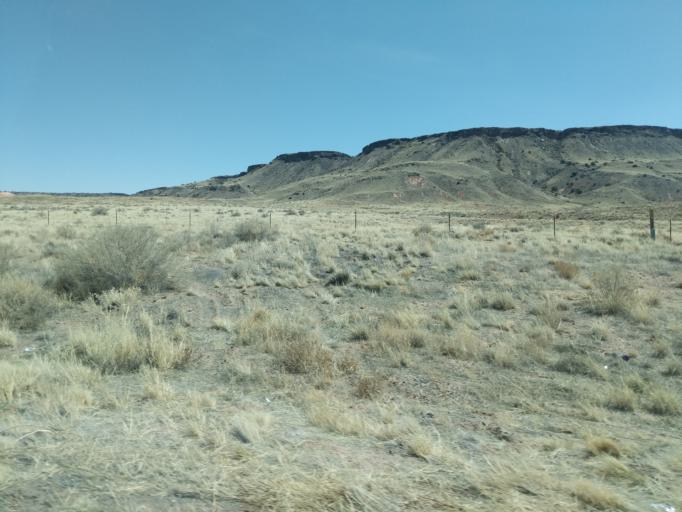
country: US
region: Arizona
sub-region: Navajo County
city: Dilkon
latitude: 35.4390
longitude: -110.0658
